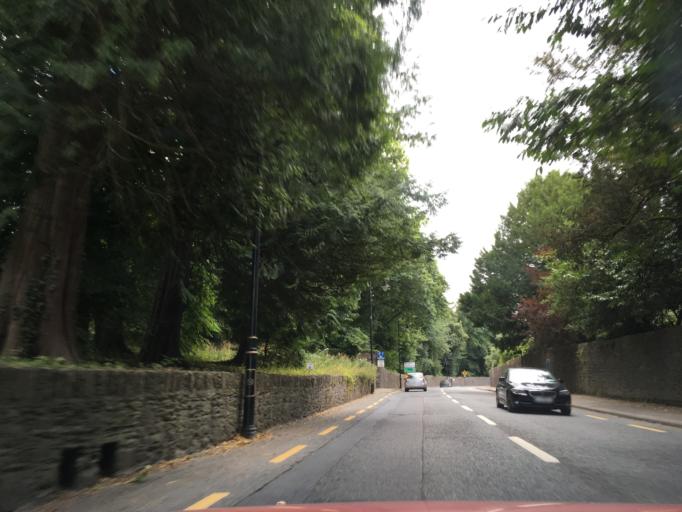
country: IE
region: Munster
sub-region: County Cork
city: Youghal
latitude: 52.1399
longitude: -7.9311
